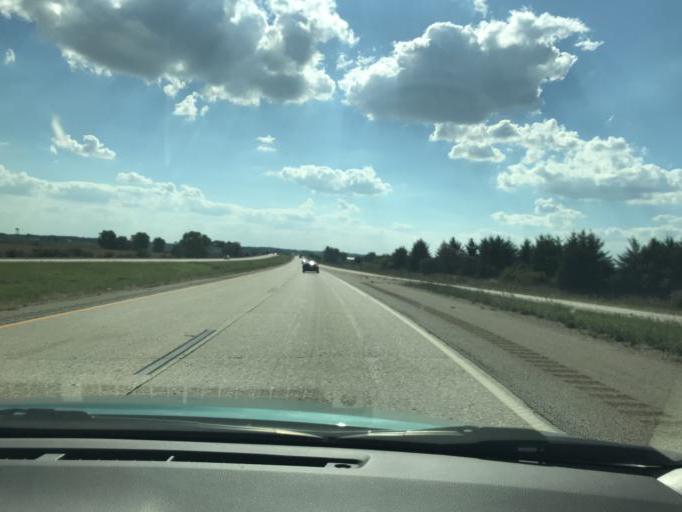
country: US
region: Wisconsin
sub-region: Walworth County
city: Darien
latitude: 42.6073
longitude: -88.7281
